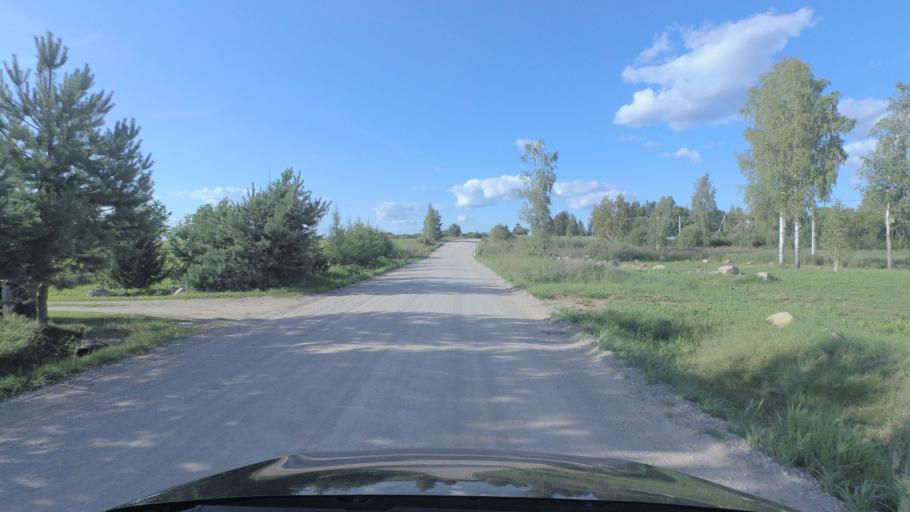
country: LT
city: Pabrade
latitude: 55.1271
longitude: 25.7051
